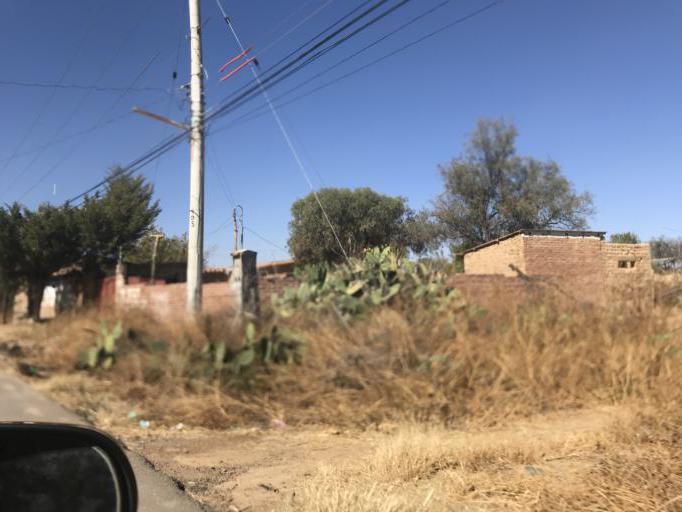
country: BO
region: Cochabamba
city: Tarata
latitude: -17.6093
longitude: -66.0074
